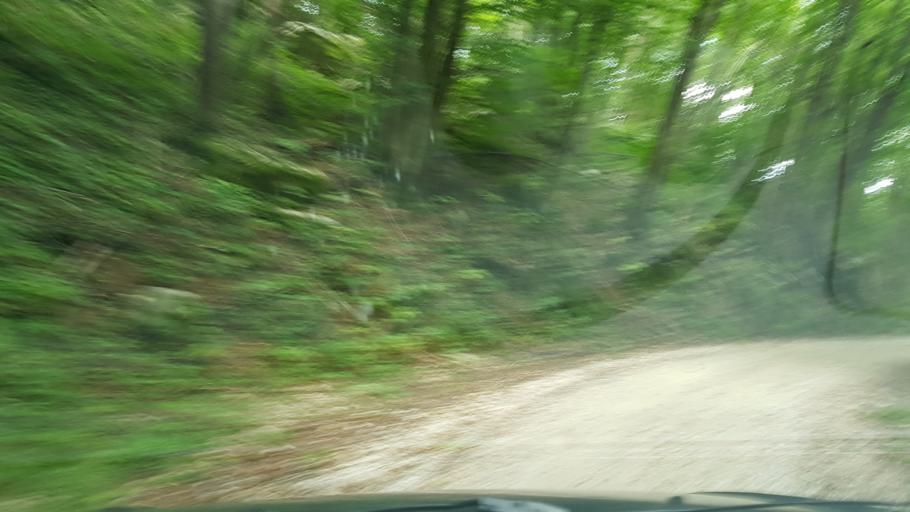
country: SI
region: Kanal
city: Deskle
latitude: 46.0572
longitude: 13.5768
